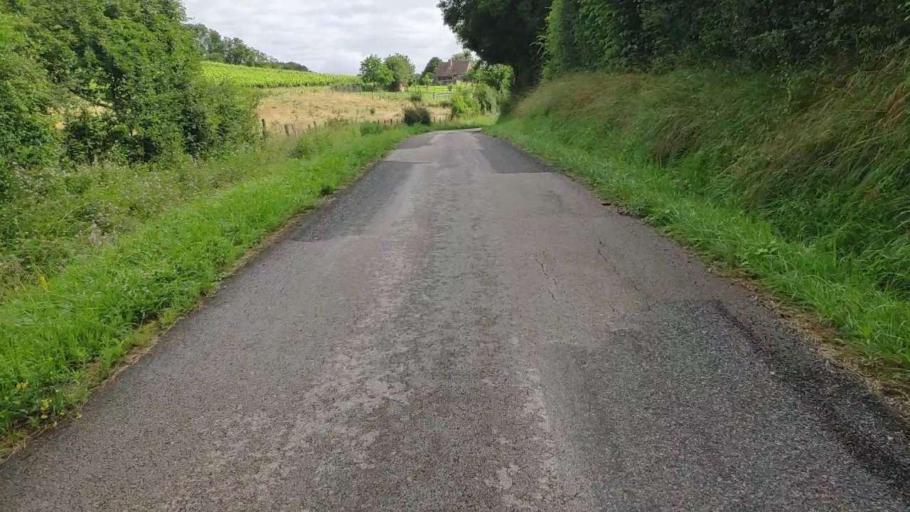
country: FR
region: Franche-Comte
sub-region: Departement du Jura
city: Poligny
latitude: 46.8283
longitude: 5.5815
